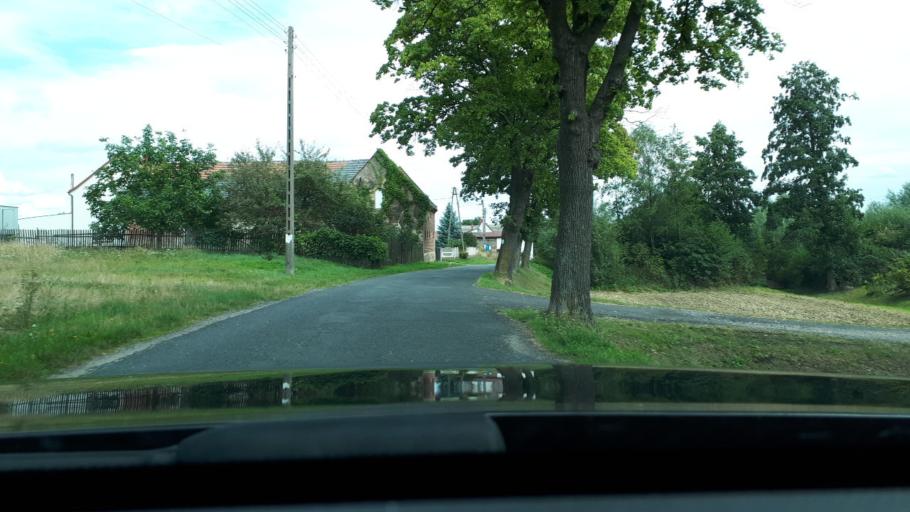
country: PL
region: Lower Silesian Voivodeship
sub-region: Powiat zlotoryjski
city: Olszanica
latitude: 51.2312
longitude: 15.8016
